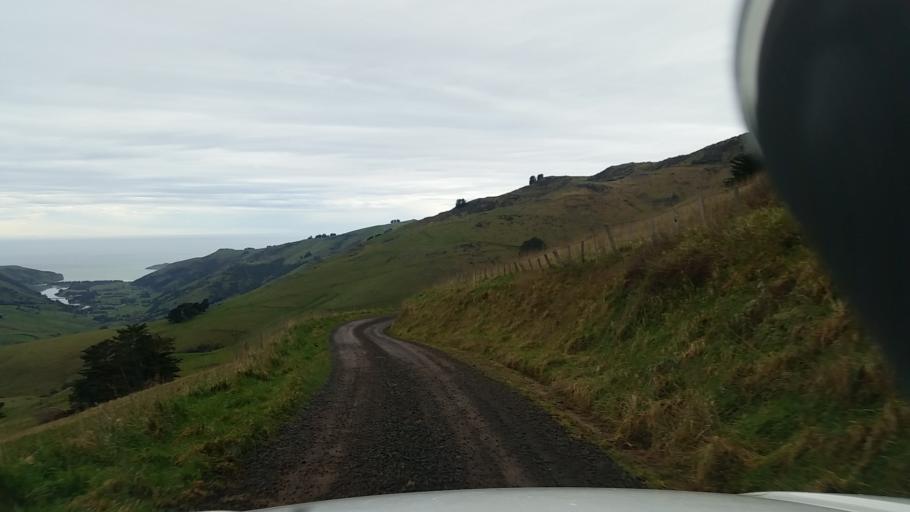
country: NZ
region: Canterbury
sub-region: Christchurch City
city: Christchurch
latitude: -43.7439
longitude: 172.9945
